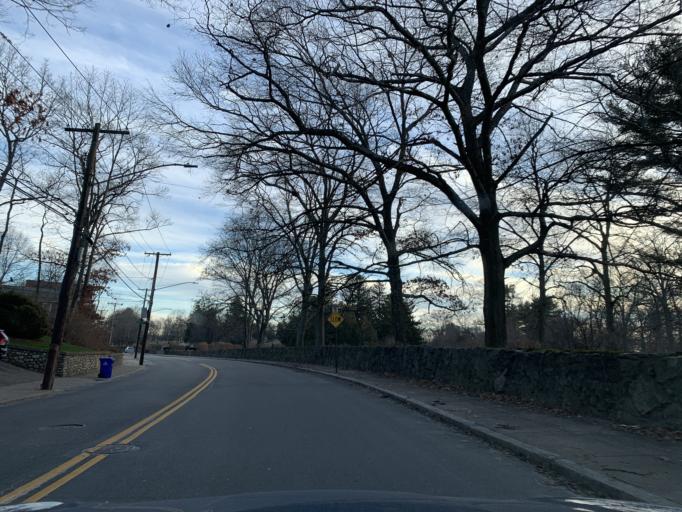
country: US
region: Massachusetts
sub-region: Norfolk County
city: Dedham
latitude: 42.2947
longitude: -71.1714
